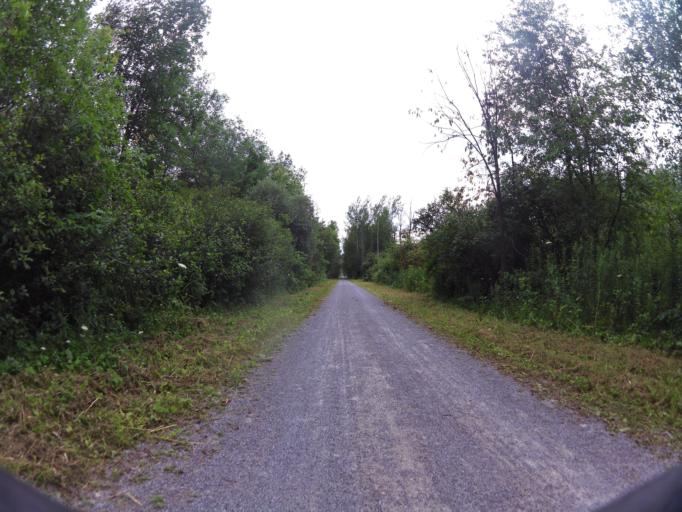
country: CA
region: Ontario
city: Ottawa
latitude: 45.1761
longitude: -75.6183
